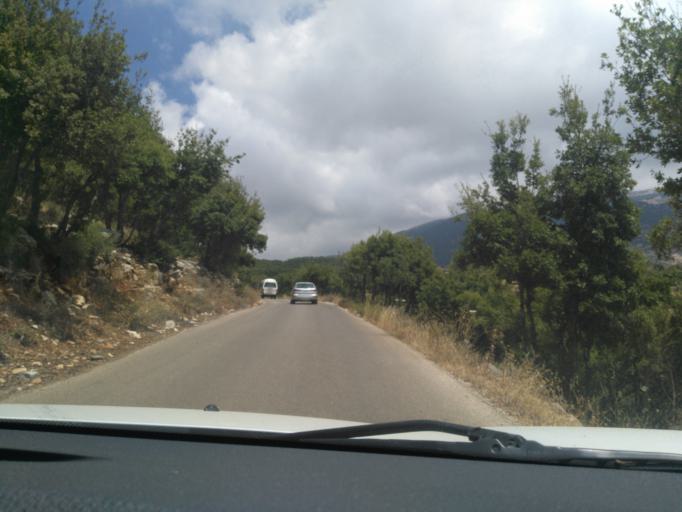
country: LB
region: Mont-Liban
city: Beit ed Dine
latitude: 33.6876
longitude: 35.6655
